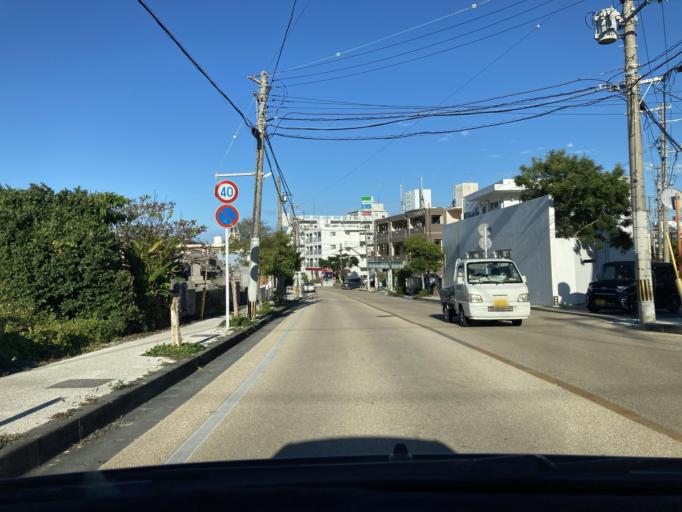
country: JP
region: Okinawa
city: Naha-shi
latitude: 26.2089
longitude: 127.7152
